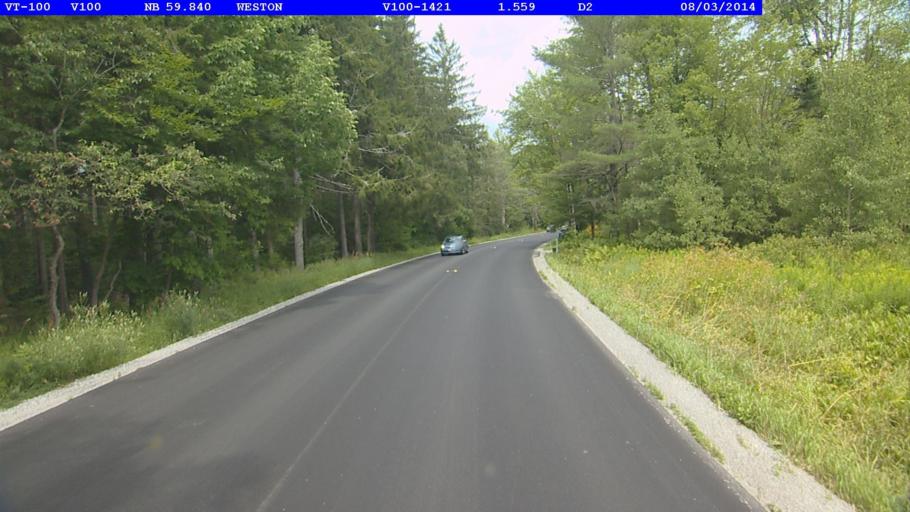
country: US
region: Vermont
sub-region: Windsor County
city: Chester
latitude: 43.2689
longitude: -72.7889
